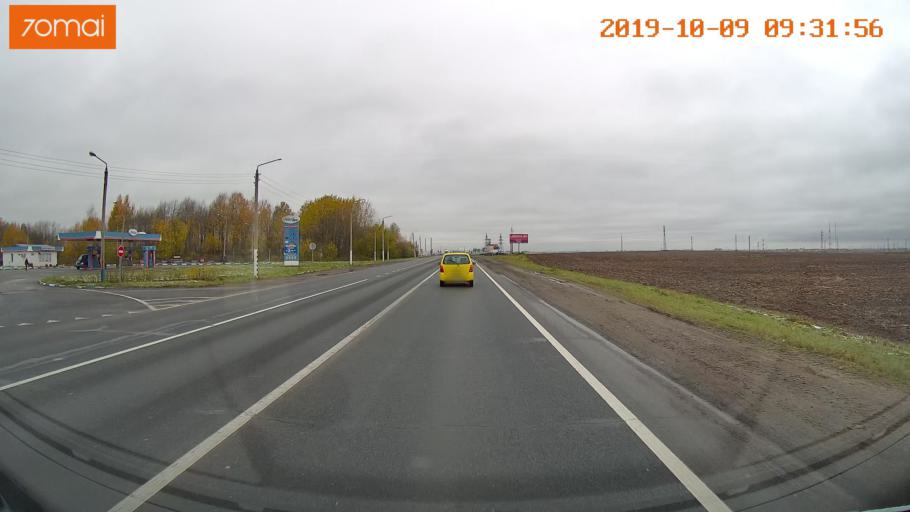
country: RU
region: Vologda
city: Vologda
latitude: 59.1531
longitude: 39.9346
